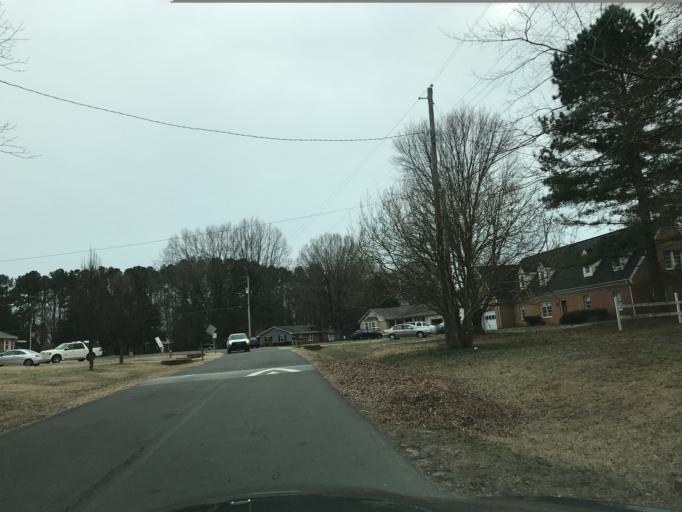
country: US
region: North Carolina
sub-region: Wake County
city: Raleigh
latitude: 35.8660
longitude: -78.6001
